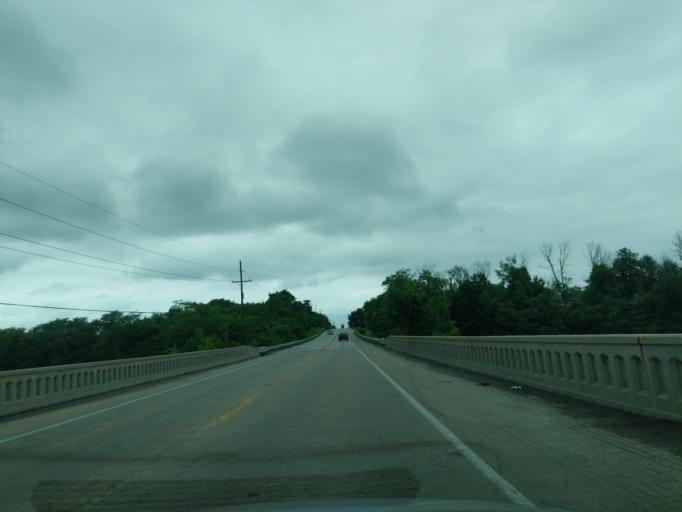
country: US
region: Indiana
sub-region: Hamilton County
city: Cicero
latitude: 40.1433
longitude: -86.0134
